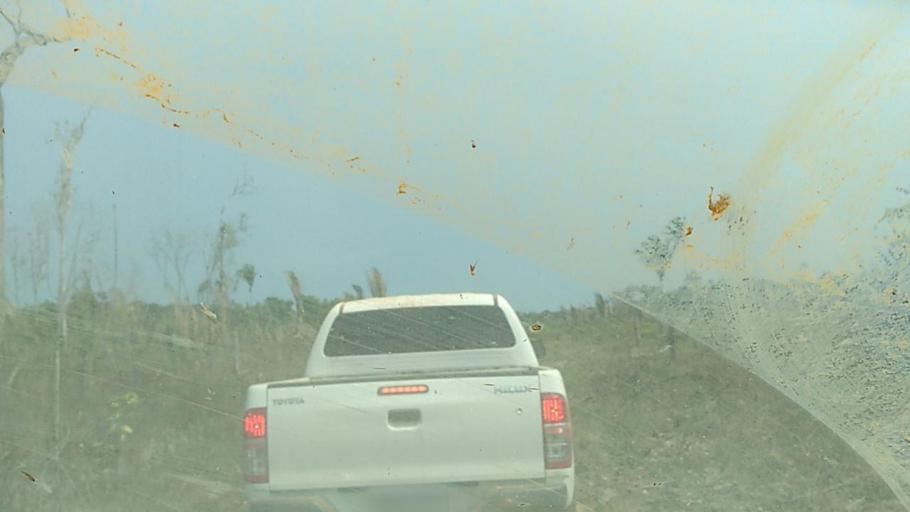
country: BR
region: Rondonia
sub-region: Porto Velho
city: Porto Velho
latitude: -8.9641
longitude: -64.3951
